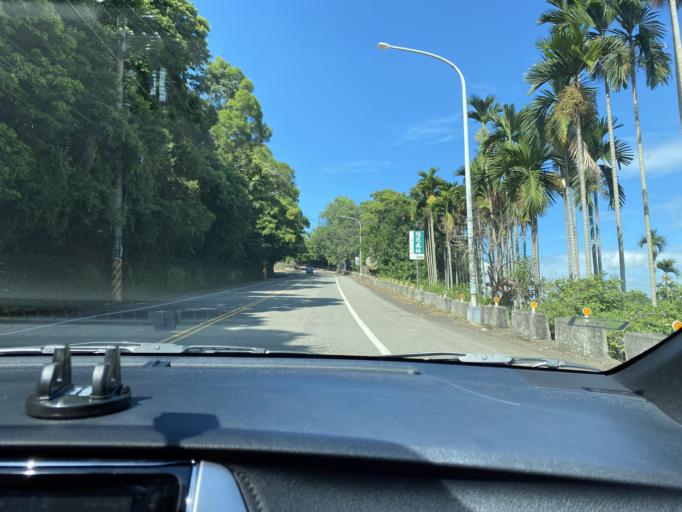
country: TW
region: Taiwan
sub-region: Nantou
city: Nantou
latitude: 23.8542
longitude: 120.6284
